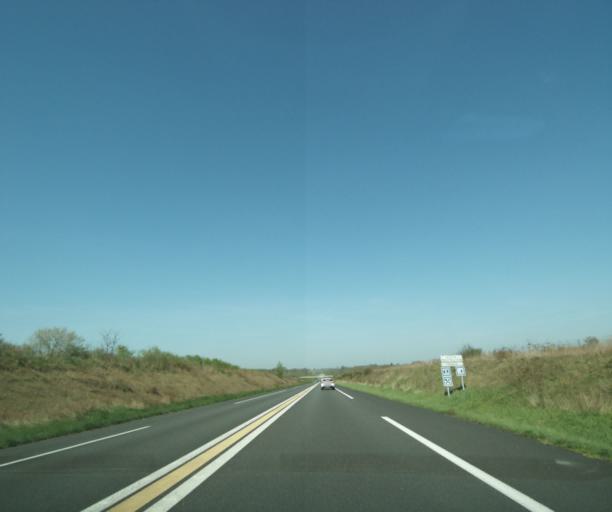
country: FR
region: Auvergne
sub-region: Departement de l'Allier
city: Diou
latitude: 46.4967
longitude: 3.7962
